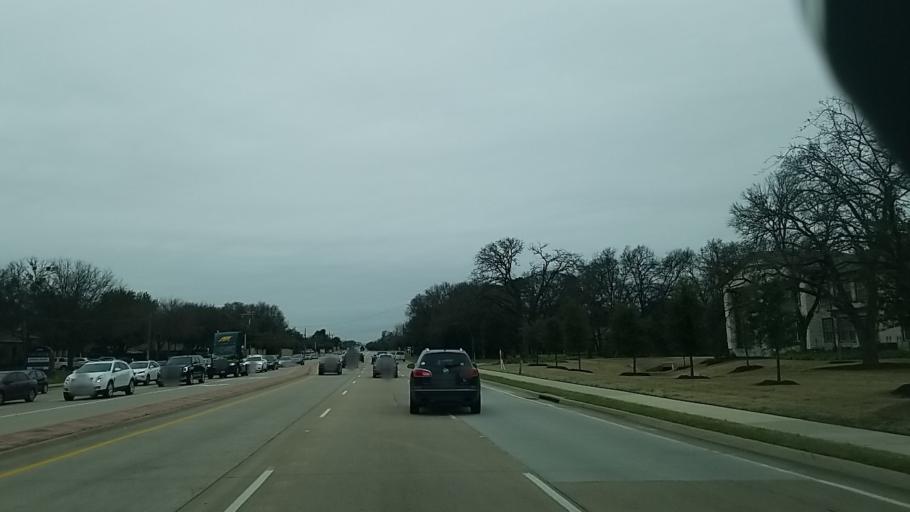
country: US
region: Texas
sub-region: Denton County
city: Flower Mound
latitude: 33.0298
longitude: -97.0709
